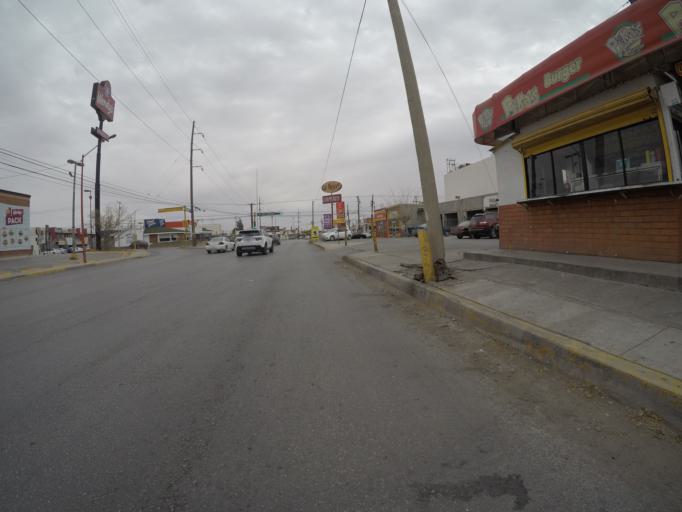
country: MX
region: Chihuahua
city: Ciudad Juarez
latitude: 31.7403
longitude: -106.4254
